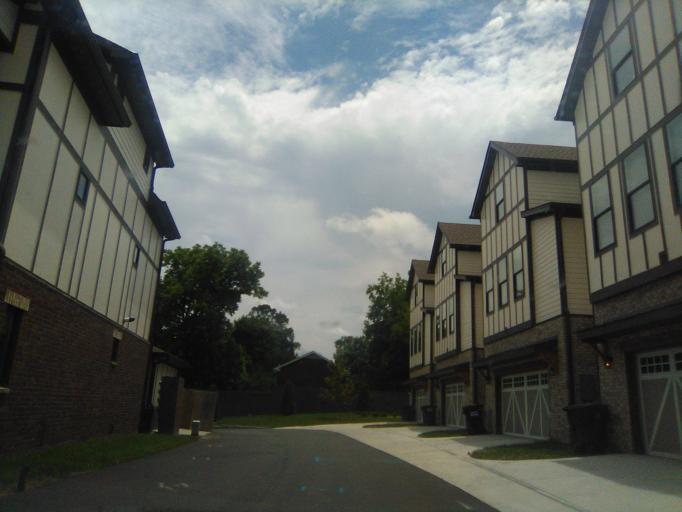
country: US
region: Tennessee
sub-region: Davidson County
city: Belle Meade
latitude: 36.1332
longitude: -86.8898
